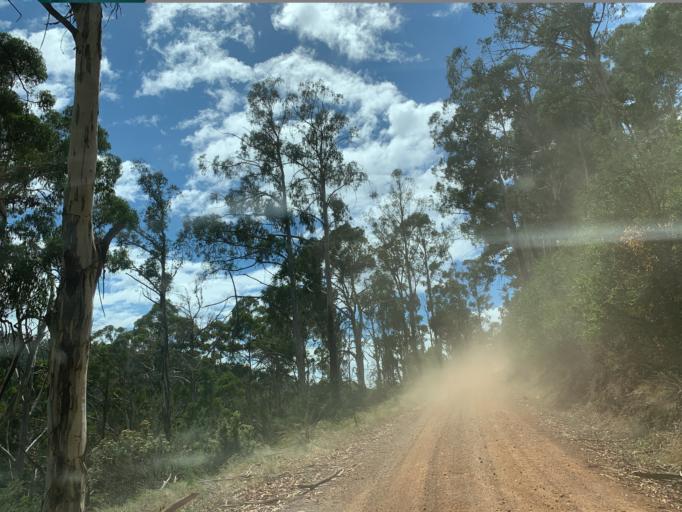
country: AU
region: Victoria
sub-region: Mansfield
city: Mansfield
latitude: -37.1012
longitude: 146.5038
